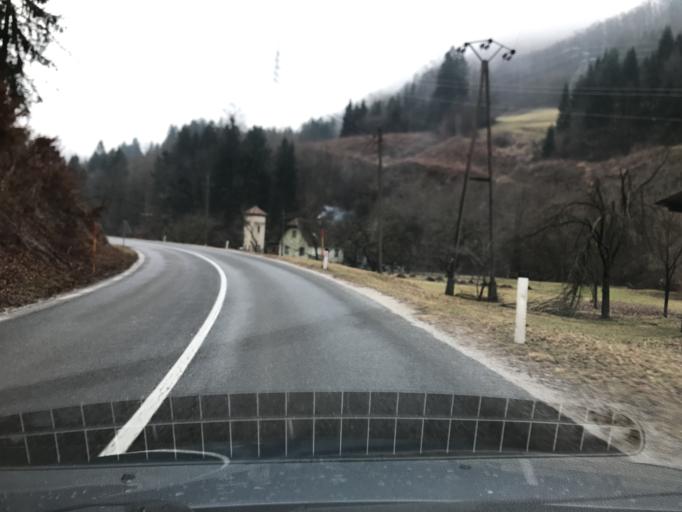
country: SI
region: Gornji Grad
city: Gornji Grad
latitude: 46.2149
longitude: 14.8467
